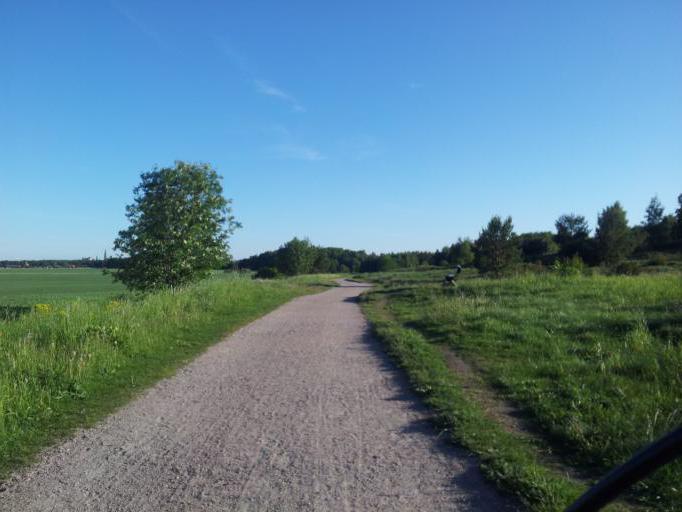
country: SE
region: Uppsala
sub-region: Uppsala Kommun
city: Gamla Uppsala
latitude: 59.8955
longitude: 17.6275
